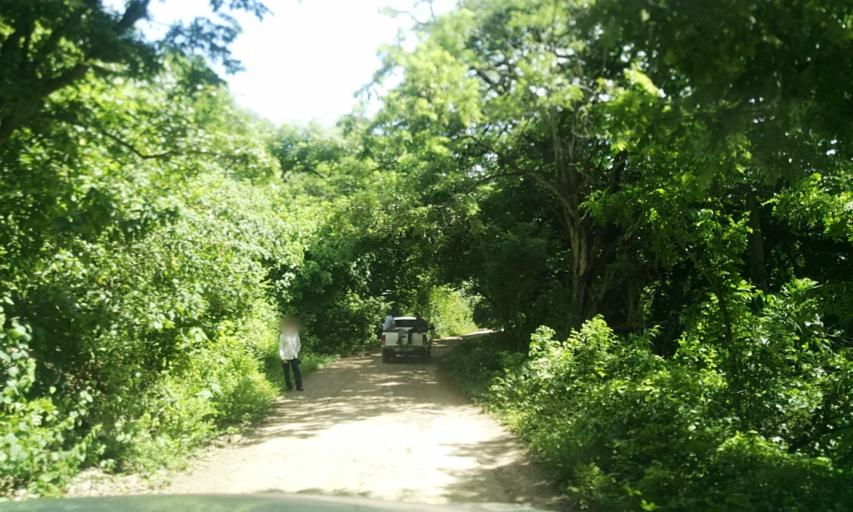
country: NI
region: Matagalpa
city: Terrabona
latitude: 12.7076
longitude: -85.9279
